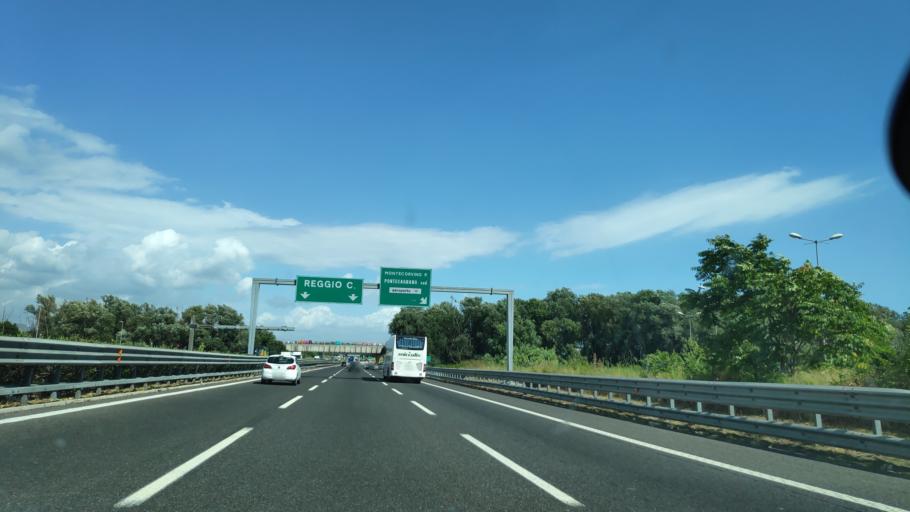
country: IT
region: Campania
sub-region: Provincia di Salerno
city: Pagliarone
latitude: 40.6360
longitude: 14.9114
